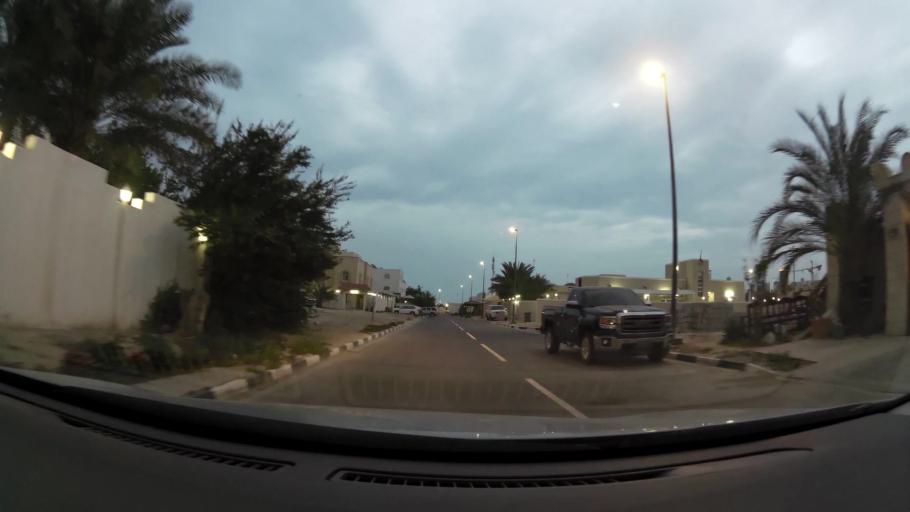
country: QA
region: Baladiyat ad Dawhah
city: Doha
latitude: 25.3463
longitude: 51.5115
